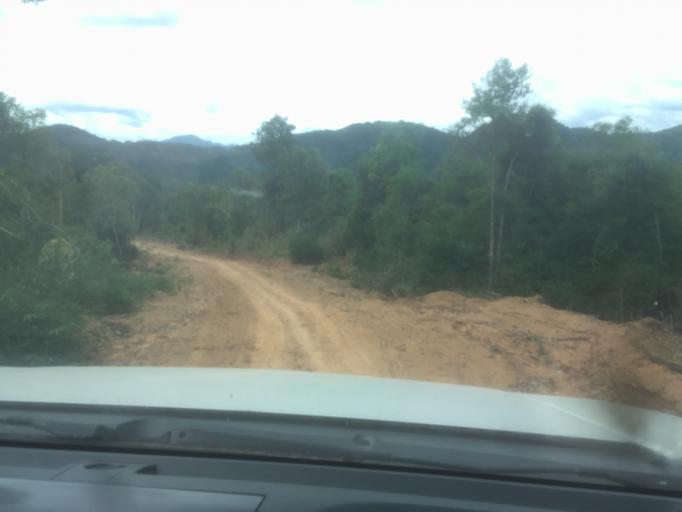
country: LA
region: Phongsali
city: Khoa
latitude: 20.9207
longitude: 102.5566
